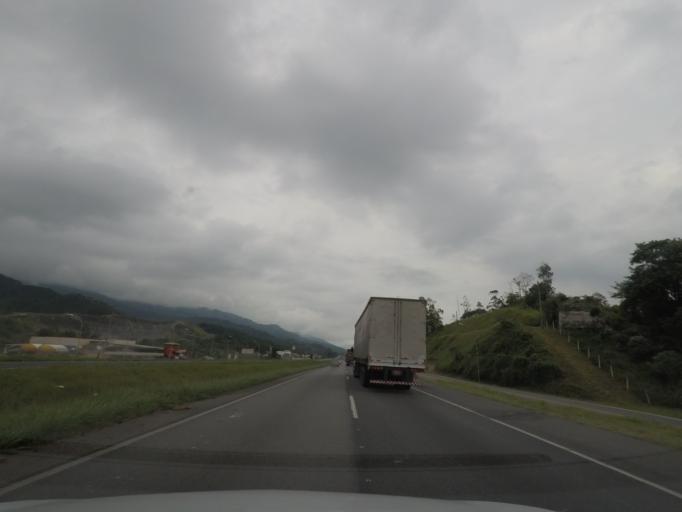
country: BR
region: Sao Paulo
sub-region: Miracatu
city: Miracatu
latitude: -24.2711
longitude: -47.4026
